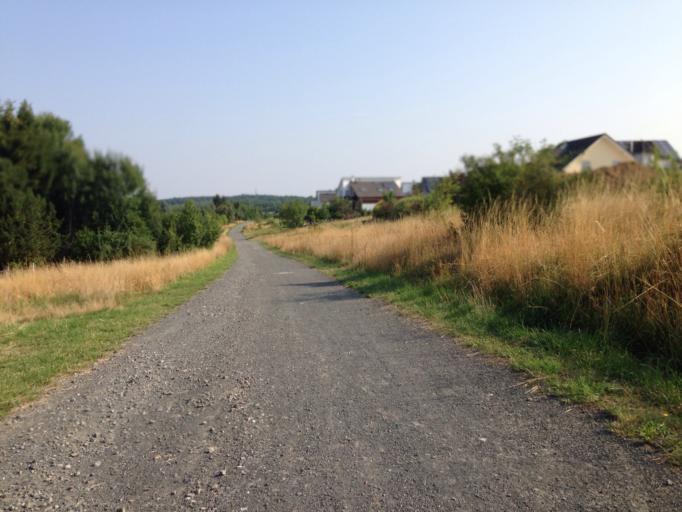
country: DE
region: Hesse
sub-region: Regierungsbezirk Giessen
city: Giessen
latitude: 50.6132
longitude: 8.6962
